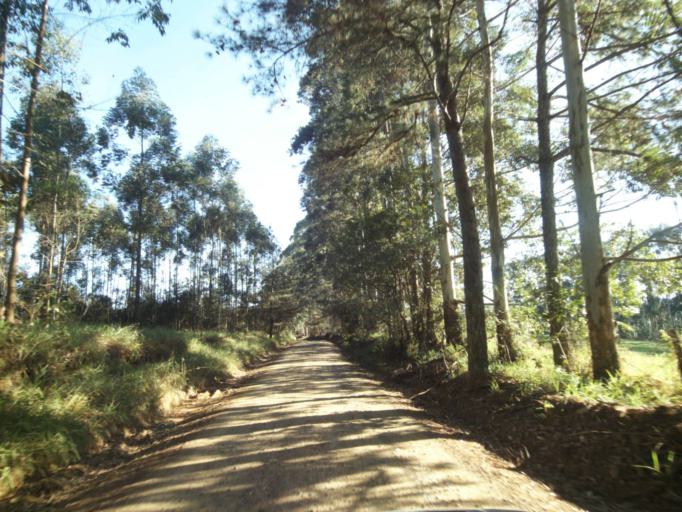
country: BR
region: Parana
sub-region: Tibagi
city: Tibagi
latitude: -24.5421
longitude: -50.6139
